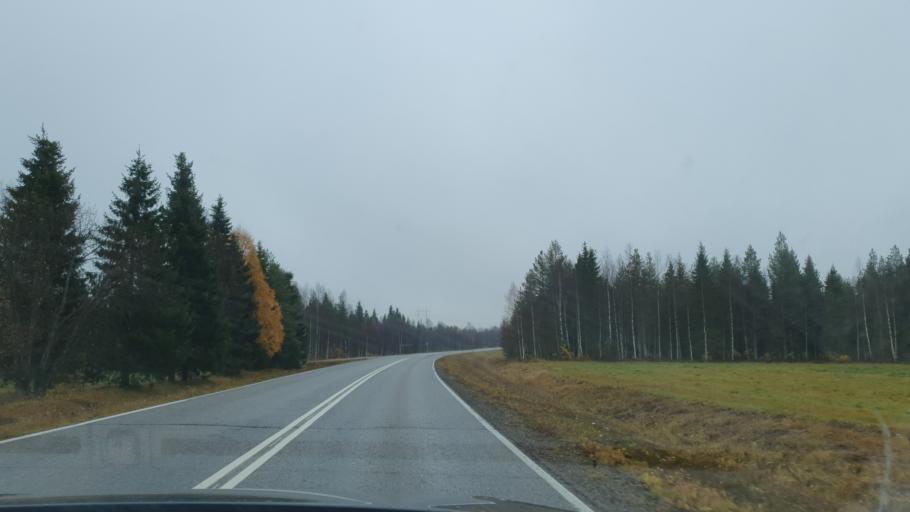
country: FI
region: Lapland
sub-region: Tunturi-Lappi
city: Kittilae
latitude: 67.4685
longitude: 24.9467
